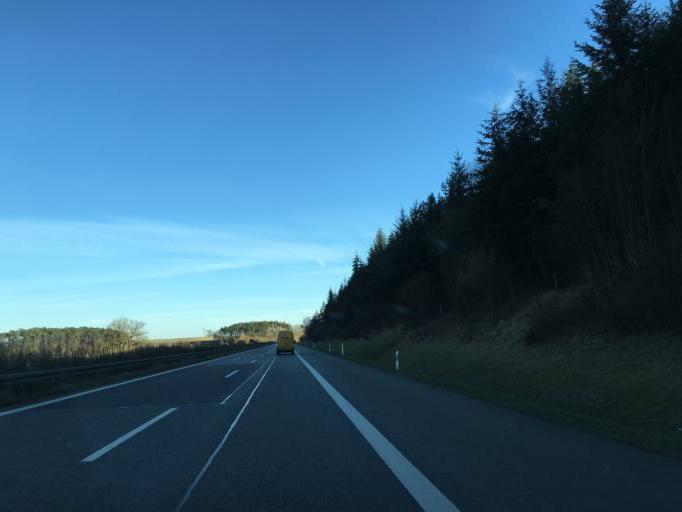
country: DE
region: Mecklenburg-Vorpommern
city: Lalendorf
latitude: 53.7324
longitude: 12.3472
